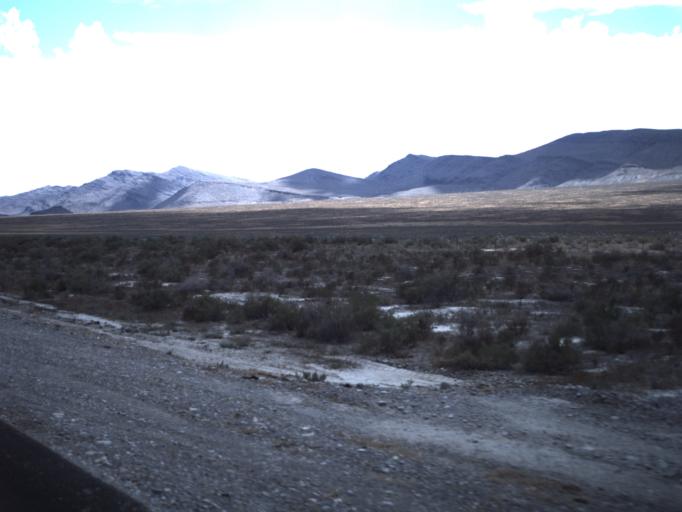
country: US
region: Utah
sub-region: Beaver County
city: Milford
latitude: 39.0791
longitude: -113.4844
